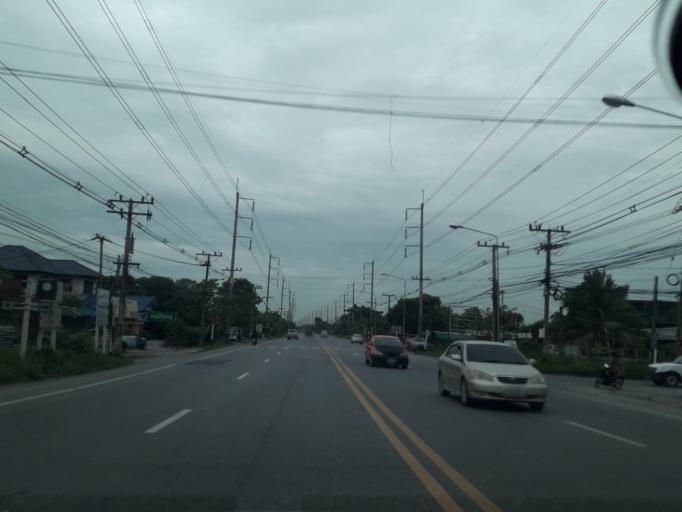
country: TH
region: Pathum Thani
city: Ban Lam Luk Ka
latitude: 13.9507
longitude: 100.8144
